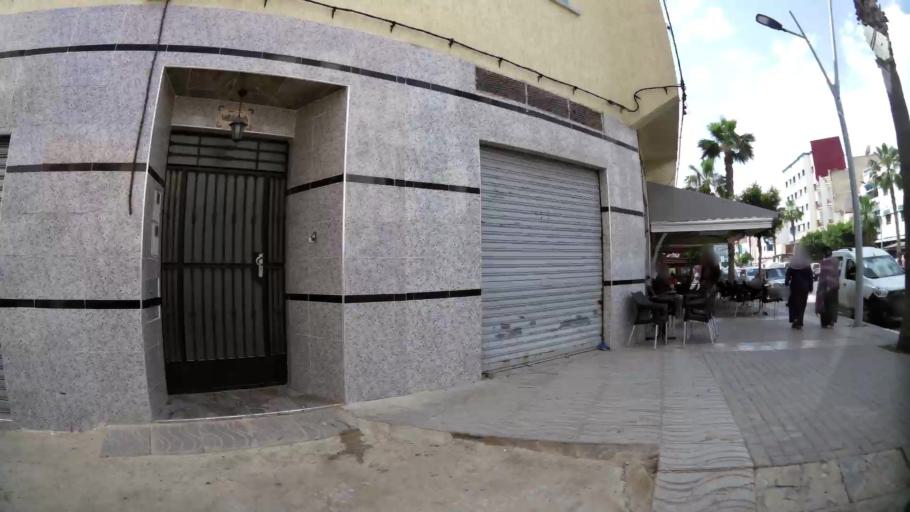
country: MA
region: Oriental
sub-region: Nador
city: Nador
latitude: 35.1662
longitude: -2.9321
